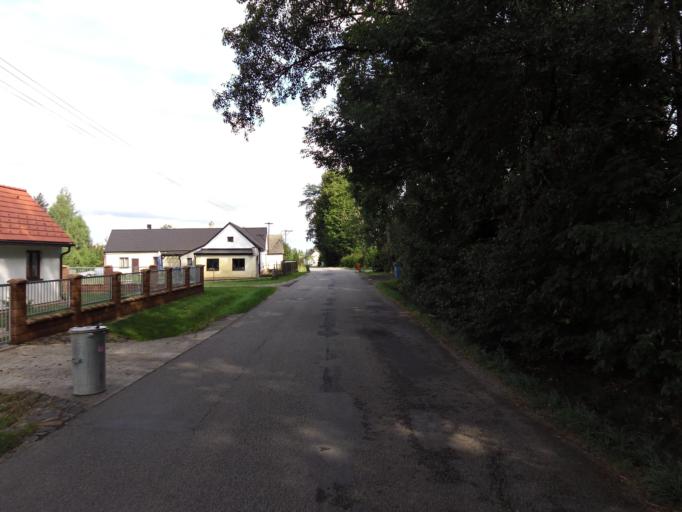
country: CZ
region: Jihocesky
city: Suchdol nad Luznici
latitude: 48.8899
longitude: 14.8489
